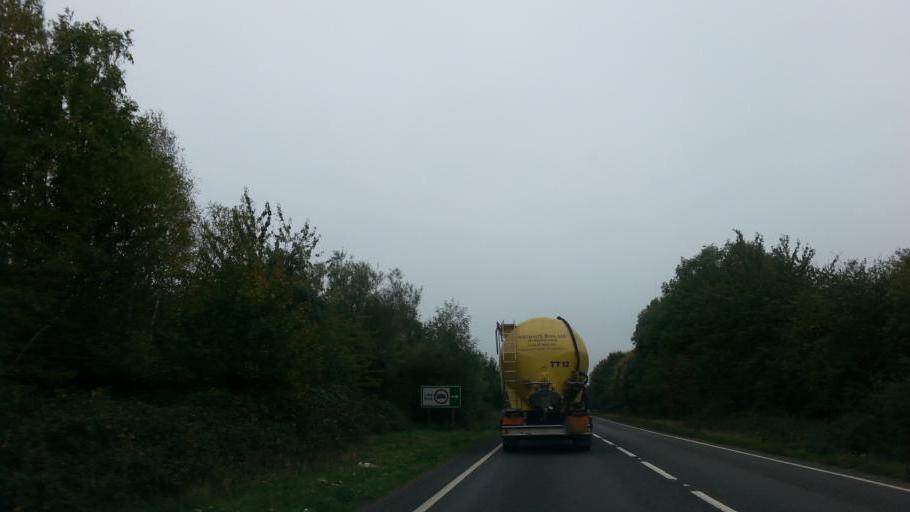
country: GB
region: England
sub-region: Northamptonshire
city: Thrapston
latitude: 52.3981
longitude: -0.5209
